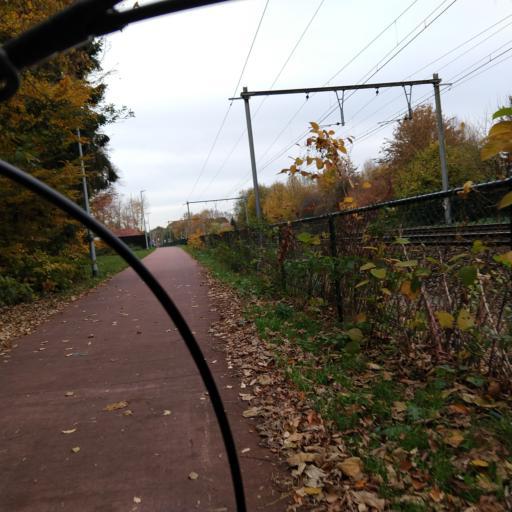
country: BE
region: Flanders
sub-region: Provincie Antwerpen
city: Kalmthout
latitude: 51.3769
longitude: 4.4668
